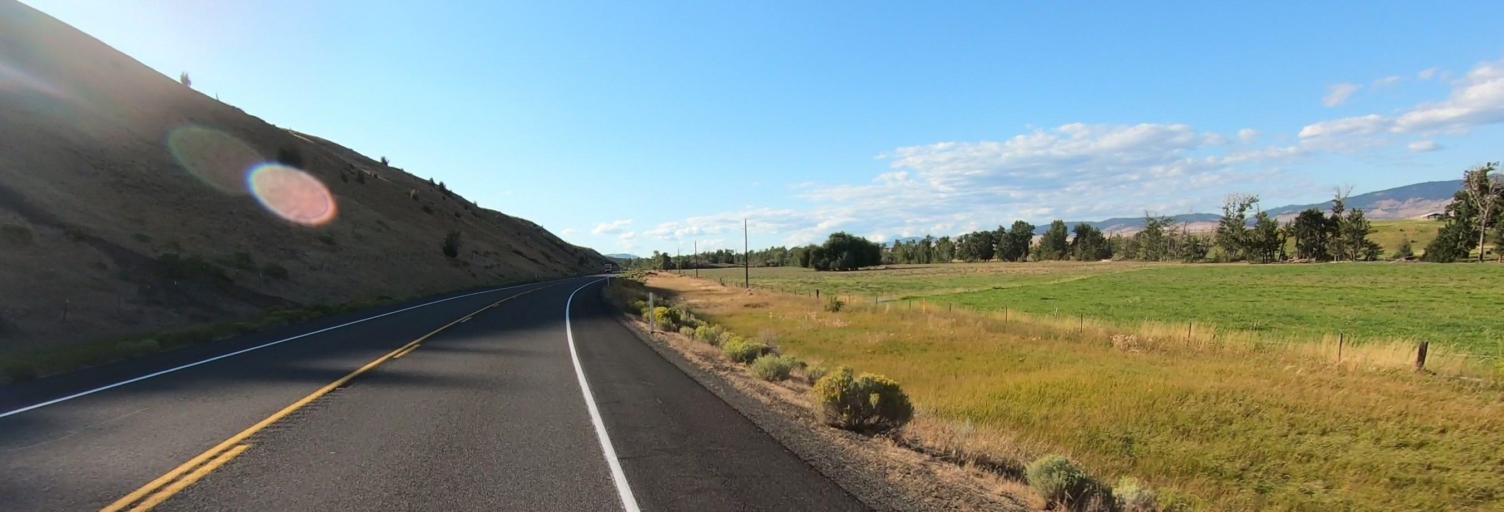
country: US
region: Washington
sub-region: Kittitas County
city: Ellensburg
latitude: 47.0763
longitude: -120.6324
